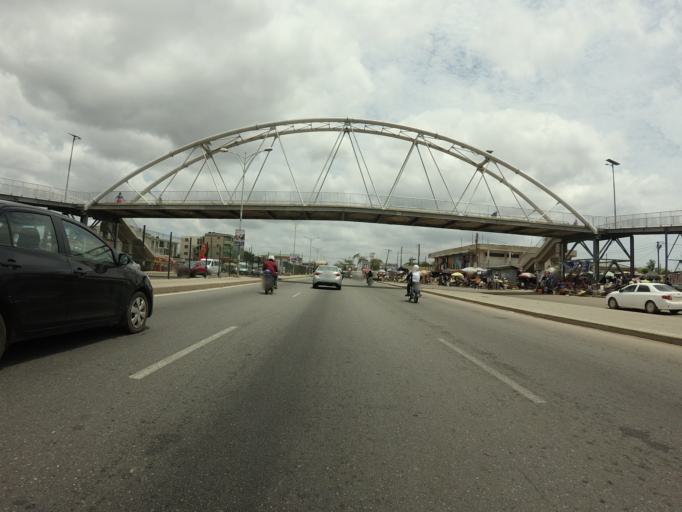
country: GH
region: Greater Accra
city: Gbawe
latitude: 5.5729
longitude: -0.2801
